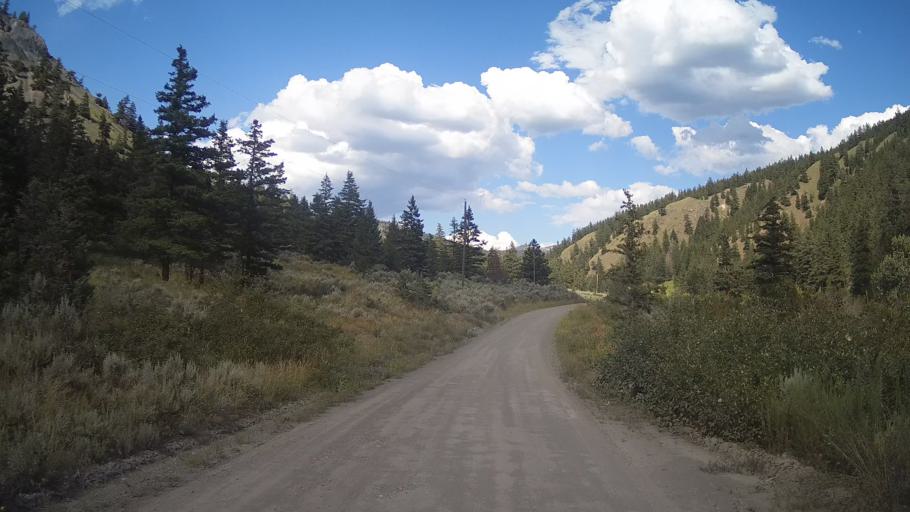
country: CA
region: British Columbia
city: Lillooet
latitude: 51.2303
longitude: -122.0576
